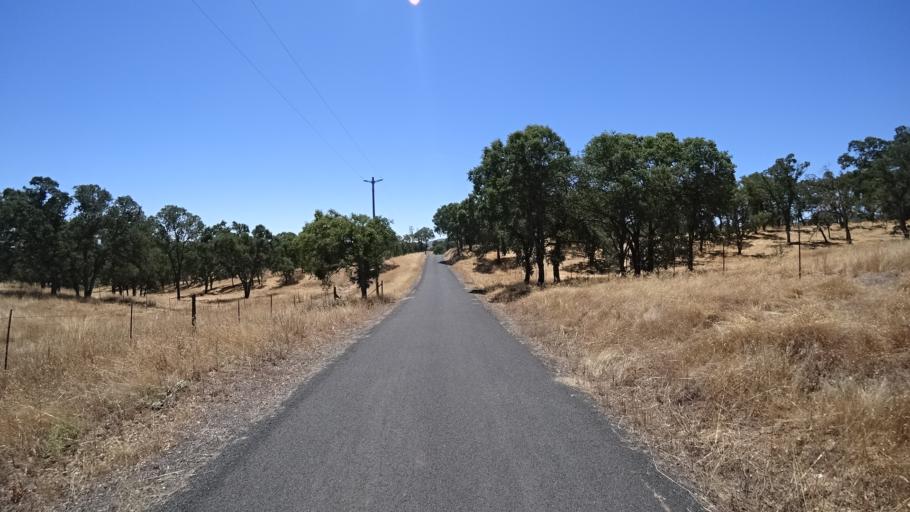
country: US
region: California
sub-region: Calaveras County
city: Copperopolis
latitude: 37.9673
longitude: -120.6742
